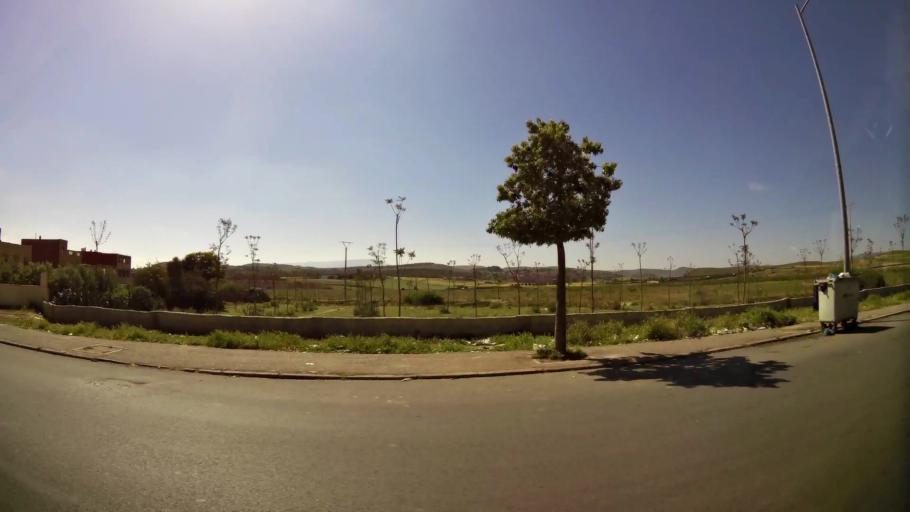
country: MA
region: Oriental
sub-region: Oujda-Angad
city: Oujda
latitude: 34.6523
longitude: -1.9366
